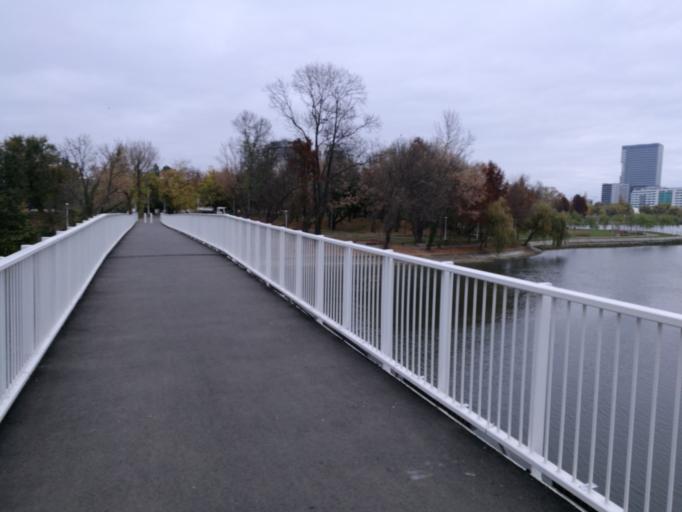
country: RO
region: Bucuresti
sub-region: Municipiul Bucuresti
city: Bucharest
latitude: 44.4736
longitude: 26.0912
